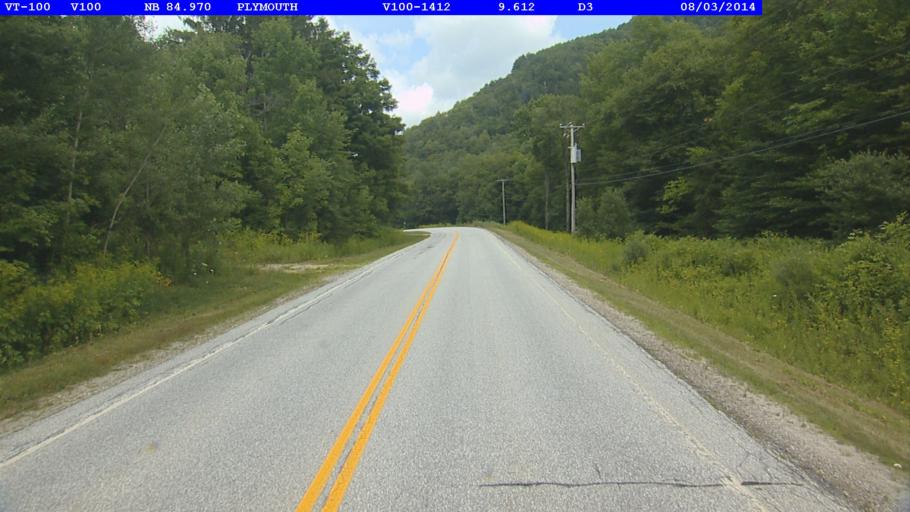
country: US
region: Vermont
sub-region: Rutland County
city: Rutland
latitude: 43.5856
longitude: -72.7571
